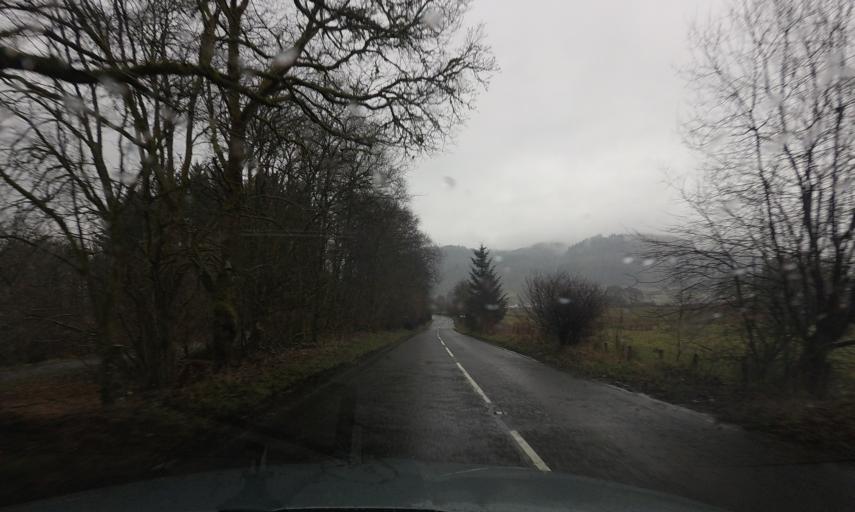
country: GB
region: Scotland
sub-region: Stirling
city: Balfron
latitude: 56.1660
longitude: -4.3648
